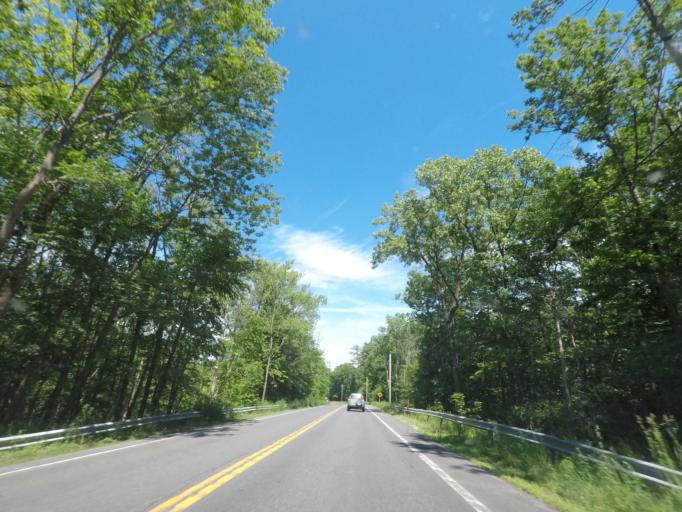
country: US
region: Massachusetts
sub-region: Berkshire County
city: West Stockbridge
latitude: 42.3358
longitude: -73.4235
